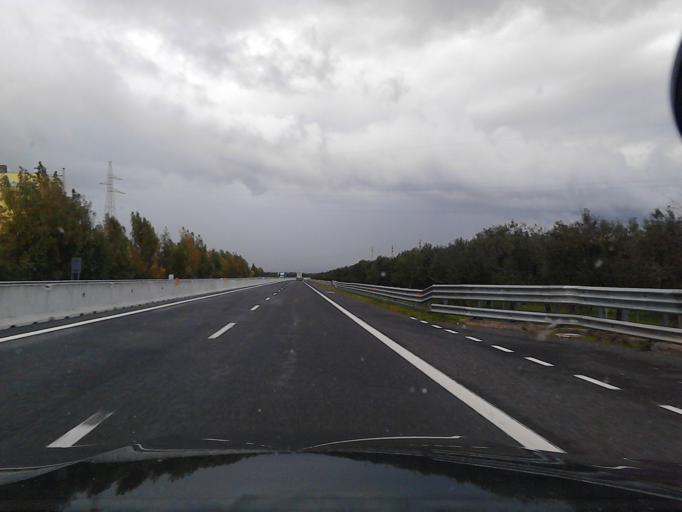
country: IT
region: Apulia
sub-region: Provincia di Bari
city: Modugno
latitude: 41.1001
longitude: 16.7562
